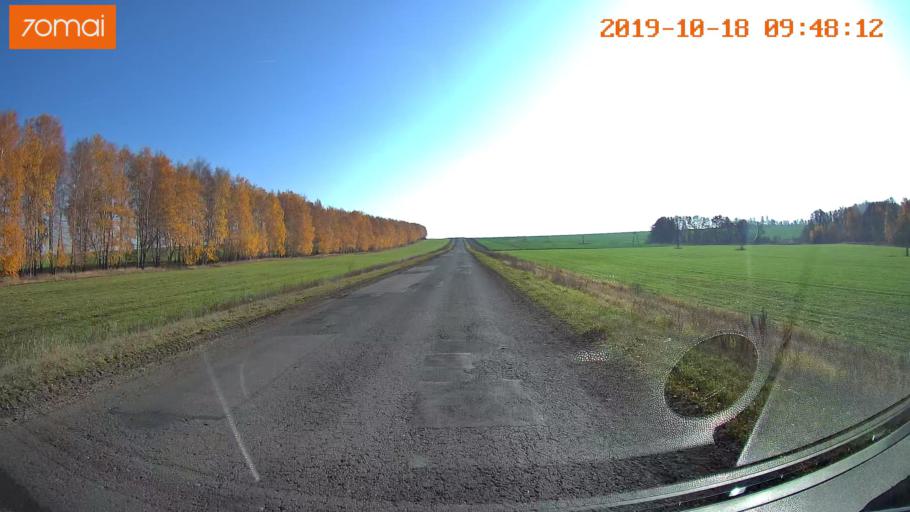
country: RU
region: Tula
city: Kazachka
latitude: 53.3189
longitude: 38.2440
